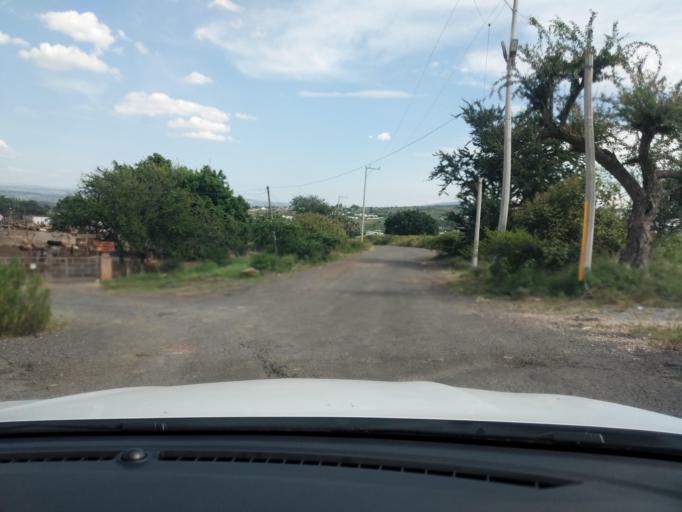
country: MX
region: Jalisco
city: Tonala
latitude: 20.6296
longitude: -103.2184
